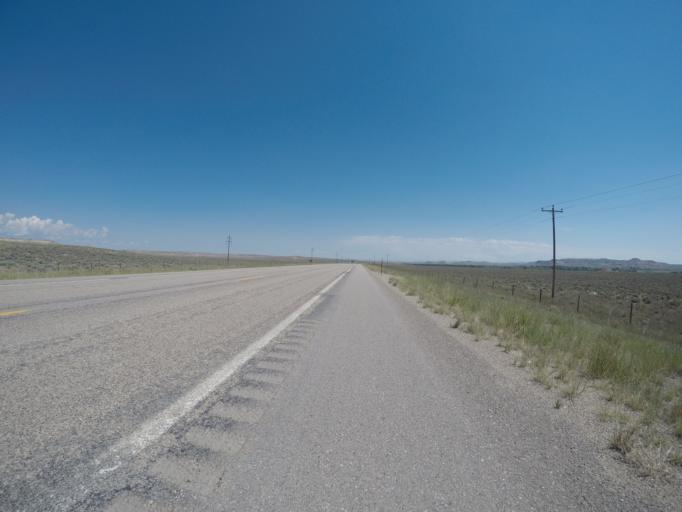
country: US
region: Wyoming
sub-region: Sublette County
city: Marbleton
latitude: 42.4066
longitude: -110.1197
